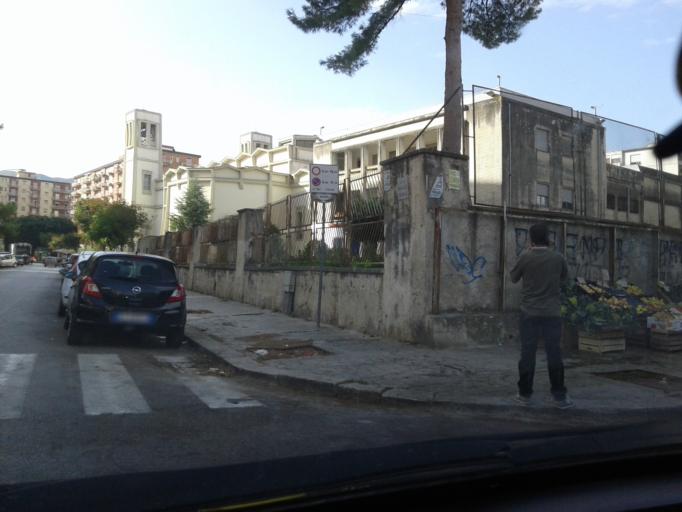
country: IT
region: Sicily
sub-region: Palermo
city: Palermo
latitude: 38.1026
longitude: 13.3342
